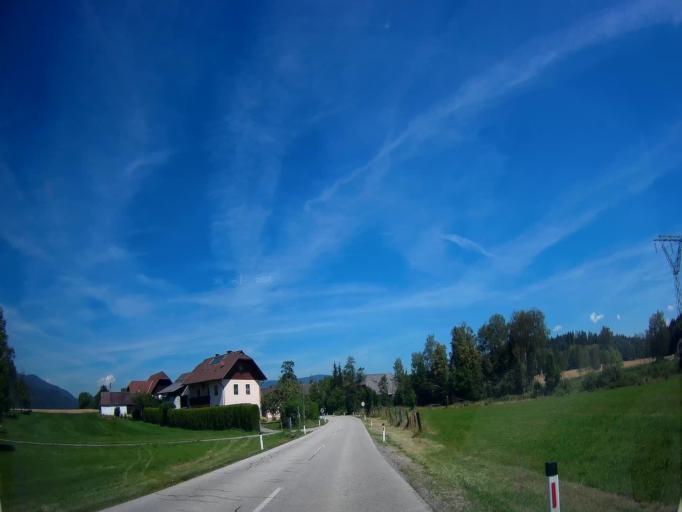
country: AT
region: Carinthia
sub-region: Politischer Bezirk Sankt Veit an der Glan
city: St. Georgen am Laengsee
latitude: 46.7993
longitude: 14.4135
